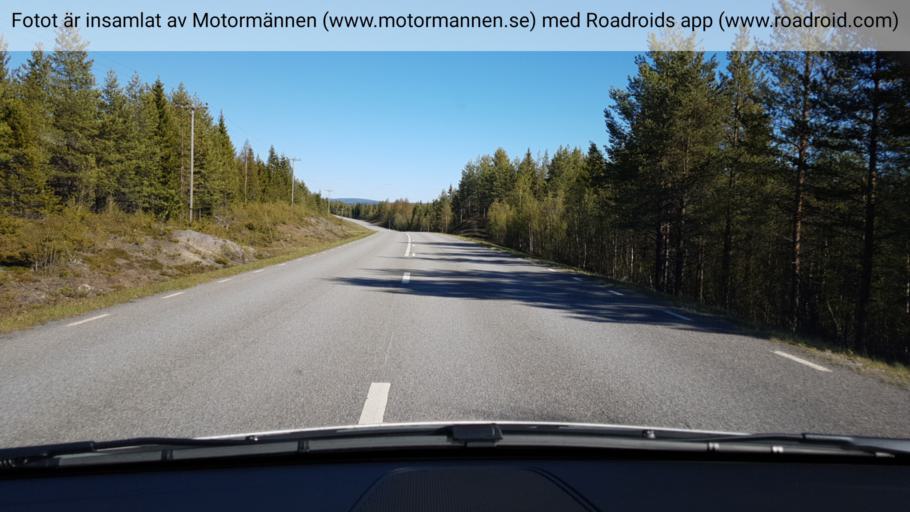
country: SE
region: Jaemtland
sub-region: Stroemsunds Kommun
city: Stroemsund
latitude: 64.2518
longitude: 15.4187
